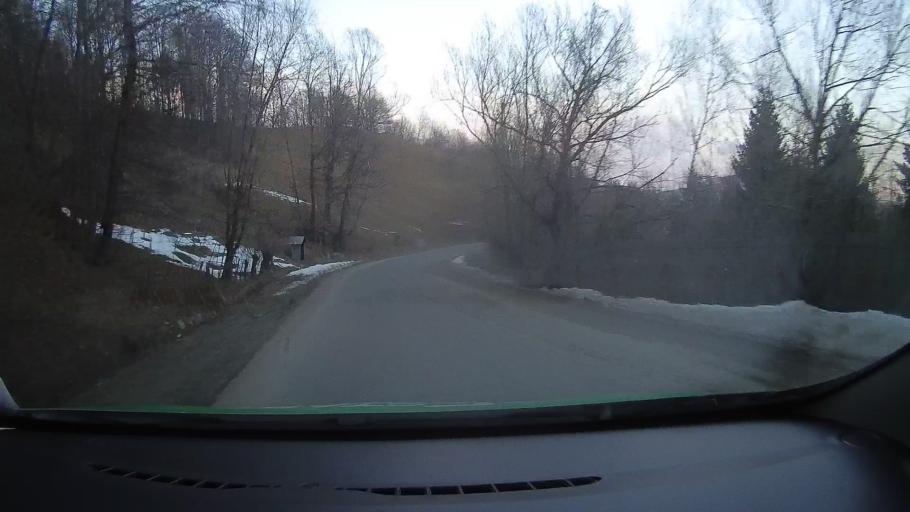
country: RO
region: Prahova
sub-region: Comuna Secaria
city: Secaria
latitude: 45.2681
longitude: 25.6755
